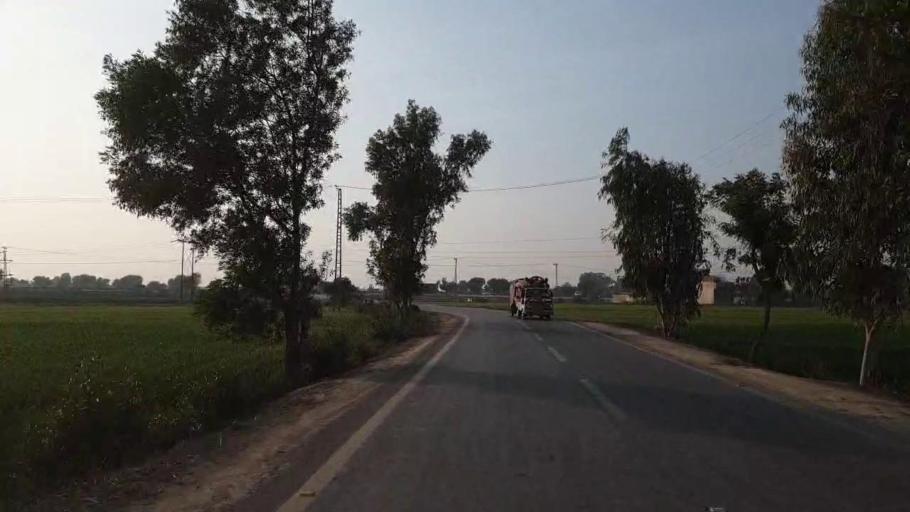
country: PK
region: Sindh
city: Matiari
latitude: 25.5872
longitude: 68.4436
